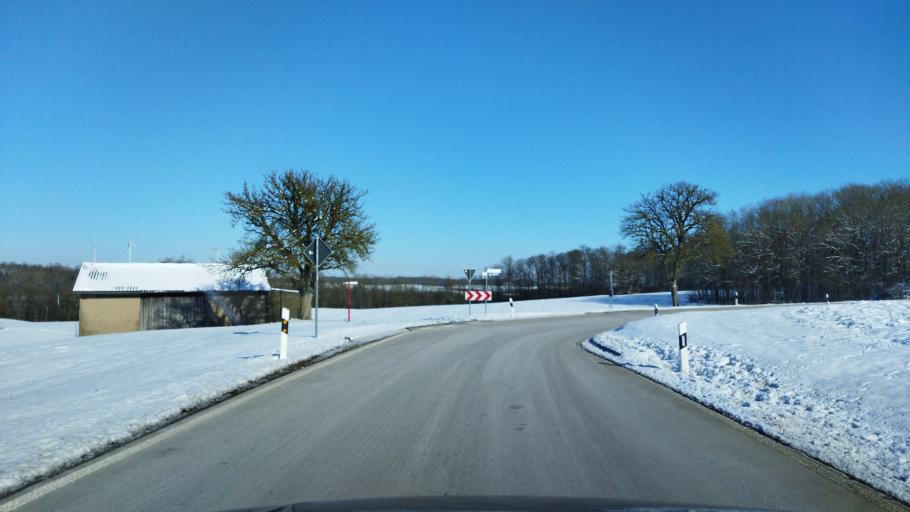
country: DE
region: Baden-Wuerttemberg
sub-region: Regierungsbezirk Stuttgart
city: Ilshofen
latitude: 49.2068
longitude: 9.9229
